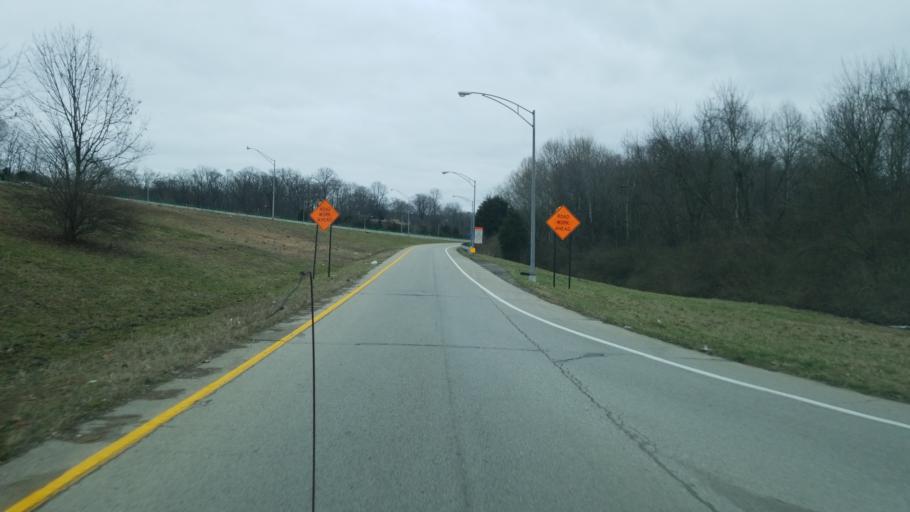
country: US
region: Kentucky
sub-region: Campbell County
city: Fort Thomas
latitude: 39.0598
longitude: -84.4204
